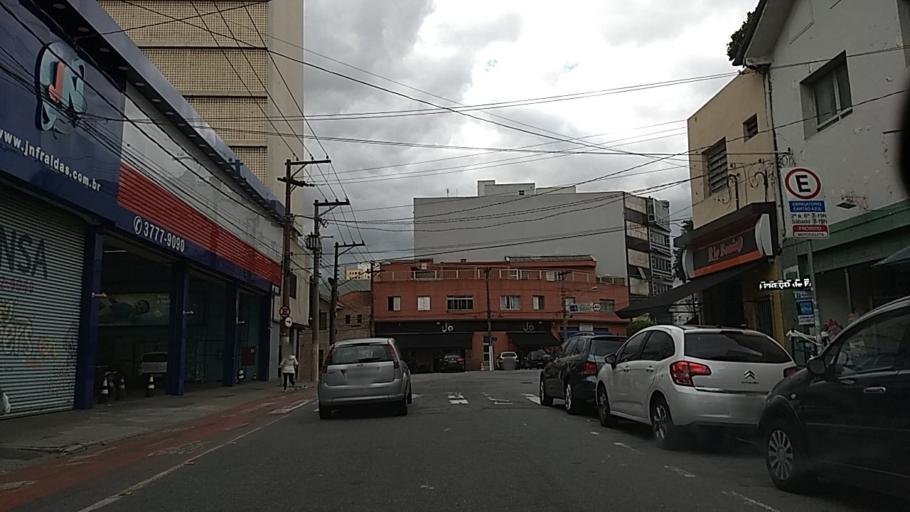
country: BR
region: Sao Paulo
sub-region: Sao Paulo
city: Sao Paulo
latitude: -23.5308
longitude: -46.6184
